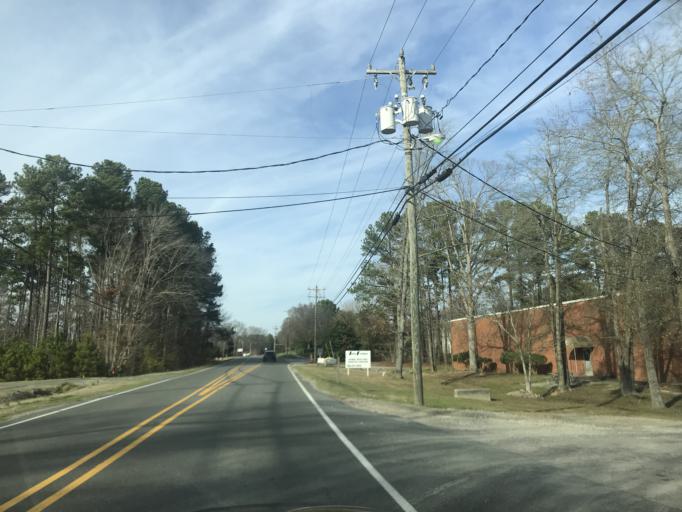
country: US
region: North Carolina
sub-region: Durham County
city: Durham
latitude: 35.9208
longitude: -78.8883
